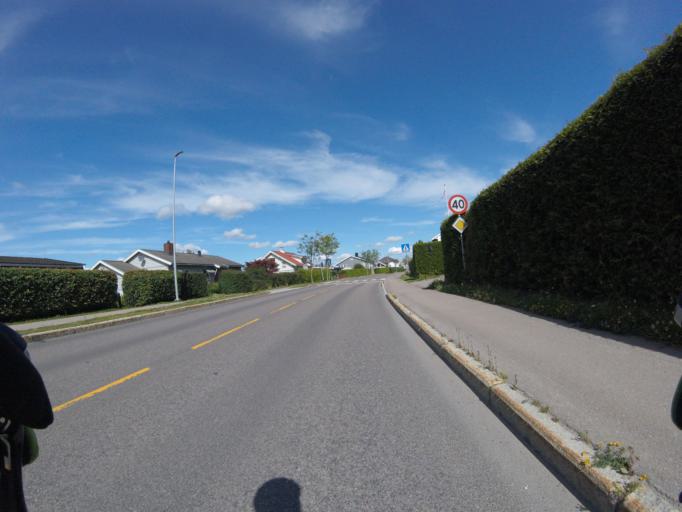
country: NO
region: Akershus
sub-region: Skedsmo
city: Lillestrom
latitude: 59.9432
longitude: 11.0161
